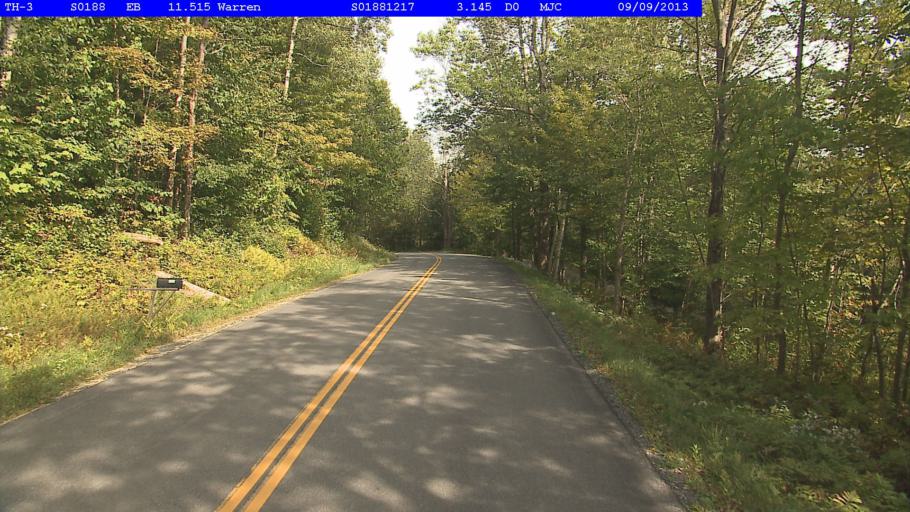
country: US
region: Vermont
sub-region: Addison County
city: Bristol
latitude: 44.1042
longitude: -72.8701
